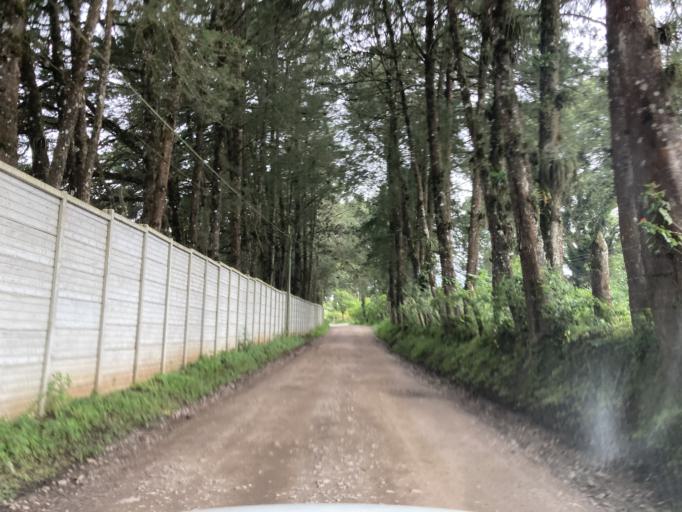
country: GT
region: Guatemala
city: San Jose Pinula
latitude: 14.5336
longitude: -90.4058
